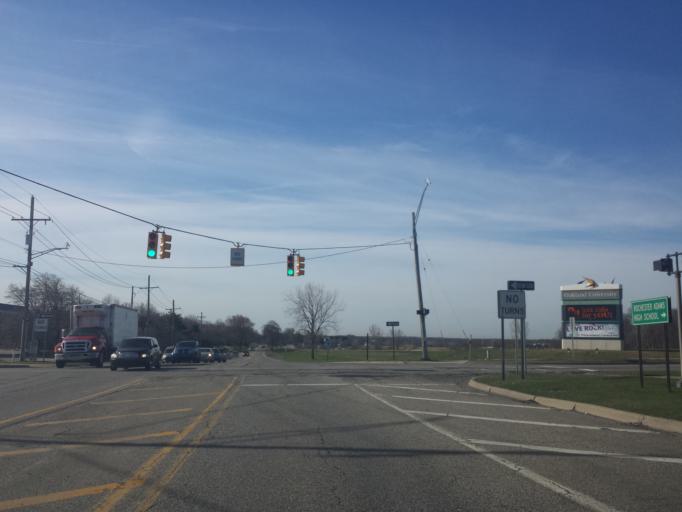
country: US
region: Michigan
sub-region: Oakland County
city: Auburn Hills
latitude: 42.6807
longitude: -83.1941
